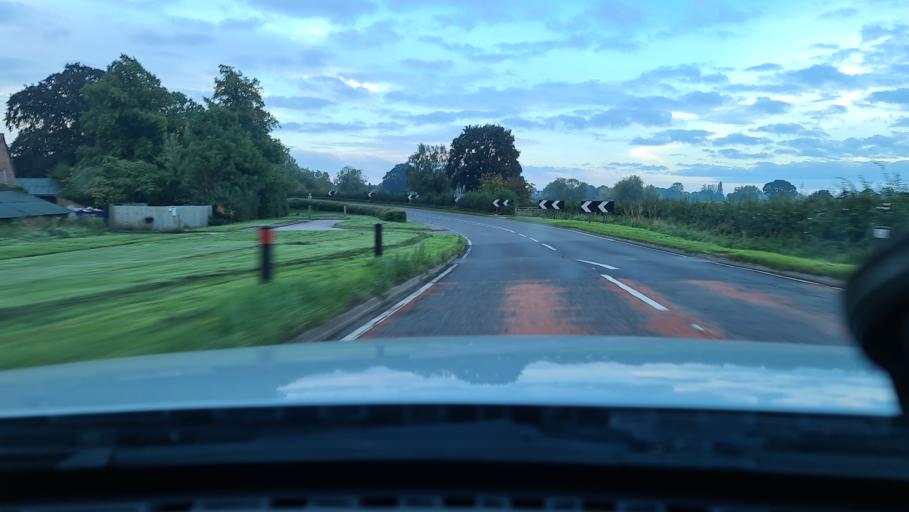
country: GB
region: England
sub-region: Warwickshire
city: Long Itchington
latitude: 52.3203
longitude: -1.4060
